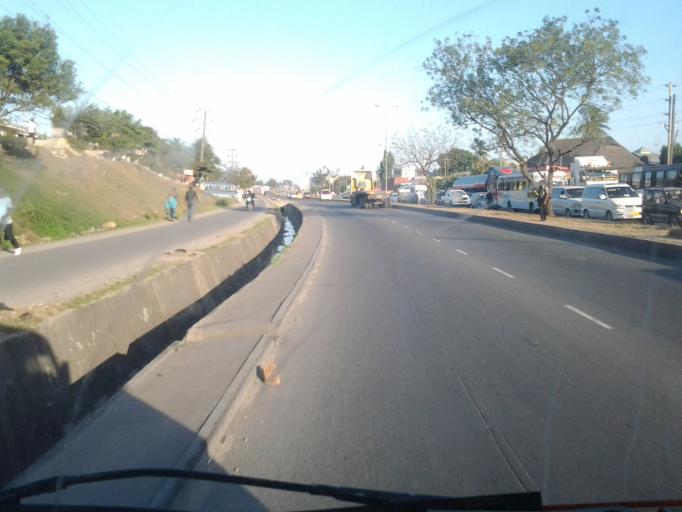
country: TZ
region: Dar es Salaam
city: Magomeni
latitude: -6.8024
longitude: 39.2080
